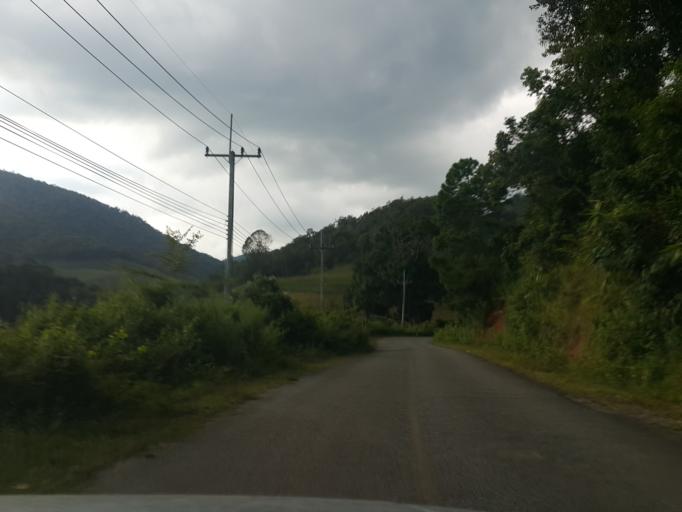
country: TH
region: Mae Hong Son
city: Khun Yuam
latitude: 18.7551
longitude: 98.1899
